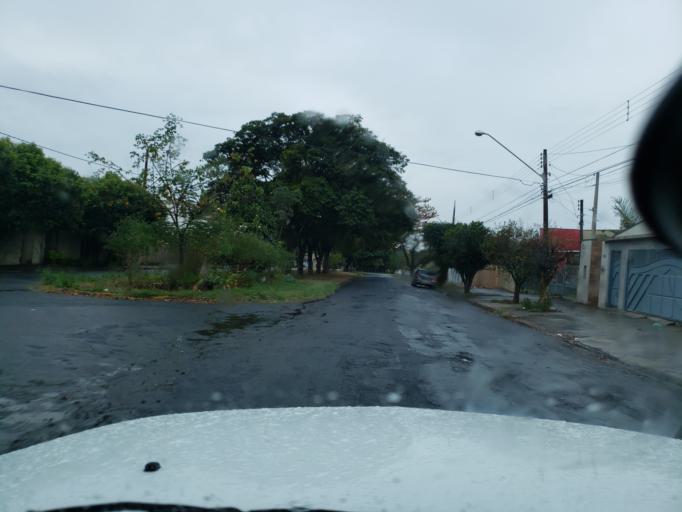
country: BR
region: Sao Paulo
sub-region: Moji-Guacu
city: Mogi-Gaucu
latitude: -22.3513
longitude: -46.9420
